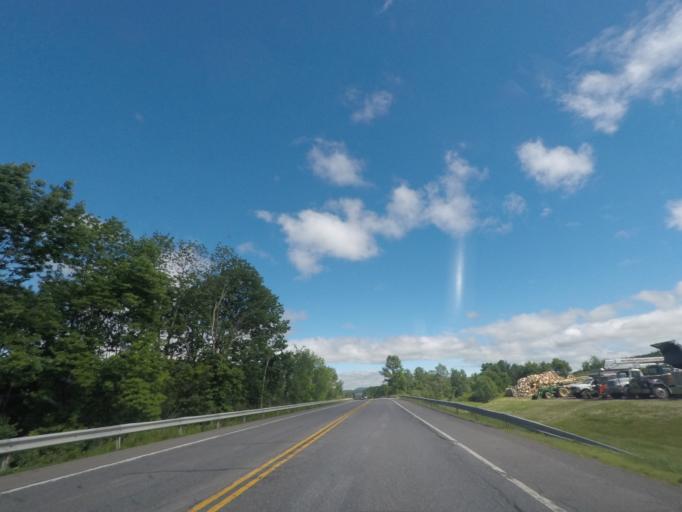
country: US
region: New York
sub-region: Columbia County
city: Philmont
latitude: 42.1852
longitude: -73.6124
